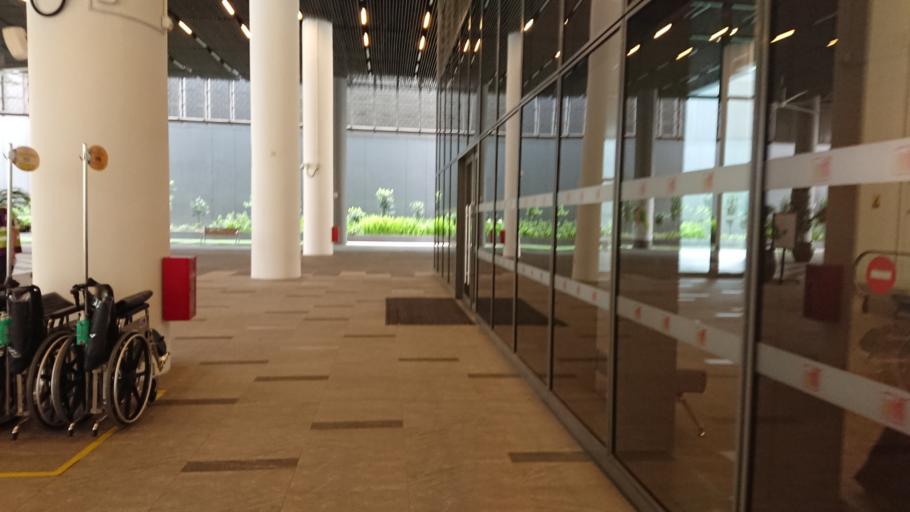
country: MY
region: Johor
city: Kampung Pasir Gudang Baru
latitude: 1.3943
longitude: 103.8932
